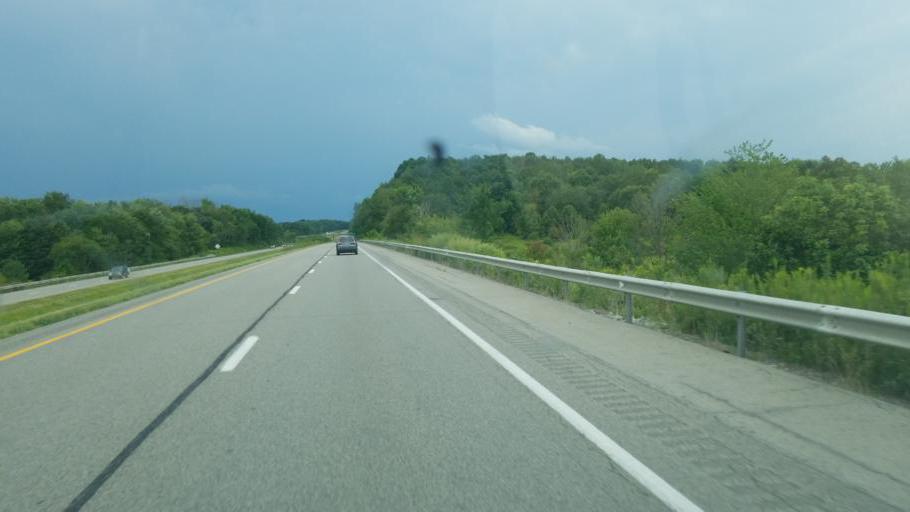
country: US
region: Pennsylvania
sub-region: Mercer County
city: Stoneboro
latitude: 41.3029
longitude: -80.1582
